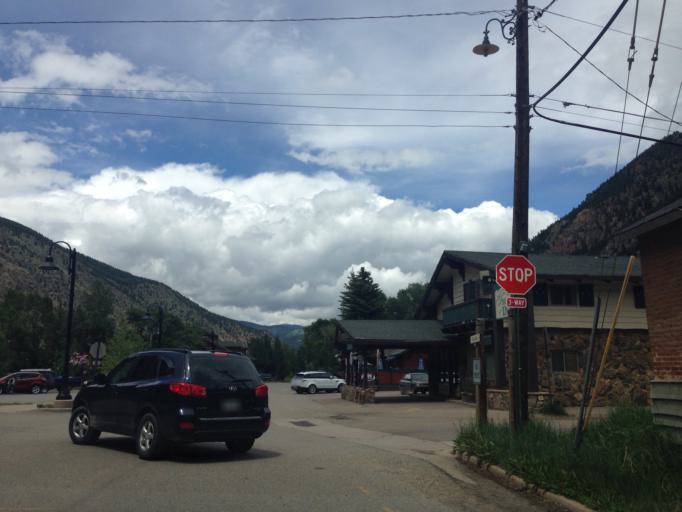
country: US
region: Colorado
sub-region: Clear Creek County
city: Georgetown
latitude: 39.7108
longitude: -105.6956
